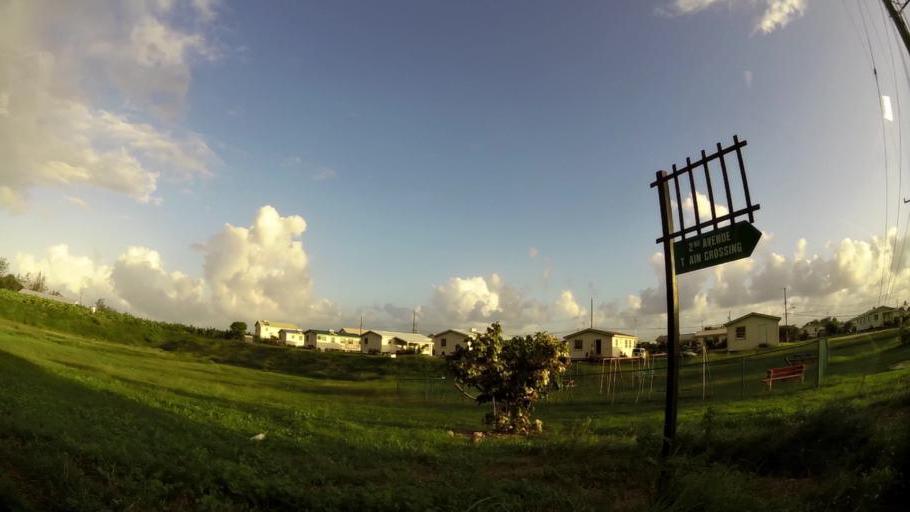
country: BB
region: Saint Philip
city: Crane
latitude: 13.1163
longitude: -59.4722
